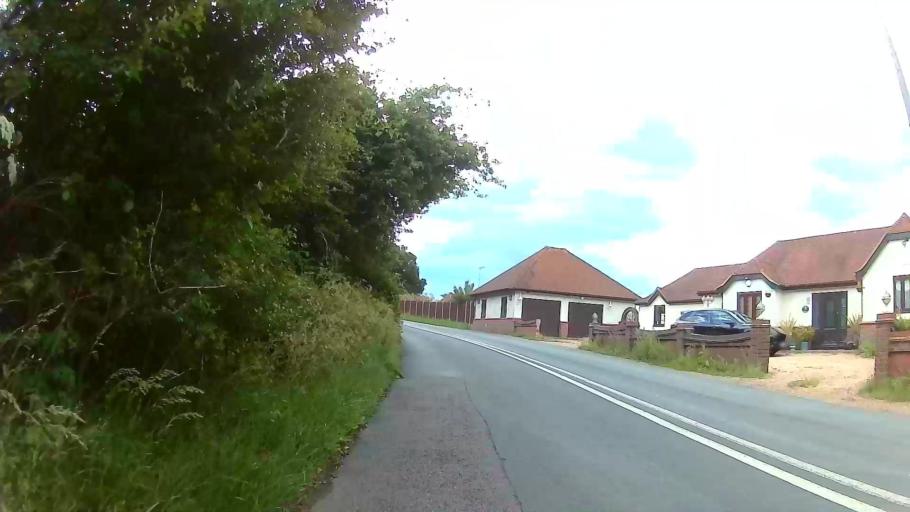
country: GB
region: England
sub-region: Greater London
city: Hainault
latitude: 51.6297
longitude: 0.1365
